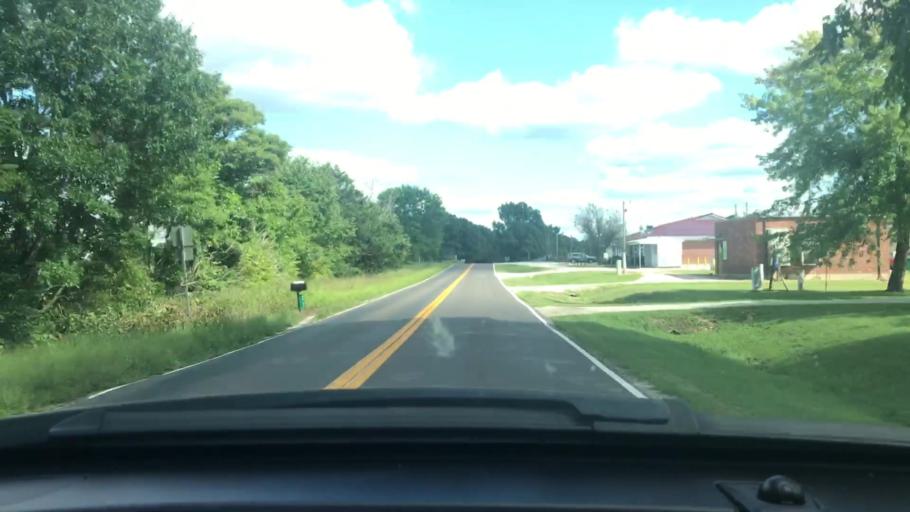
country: US
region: Missouri
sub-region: Wright County
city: Hartville
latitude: 37.3791
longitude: -92.3605
